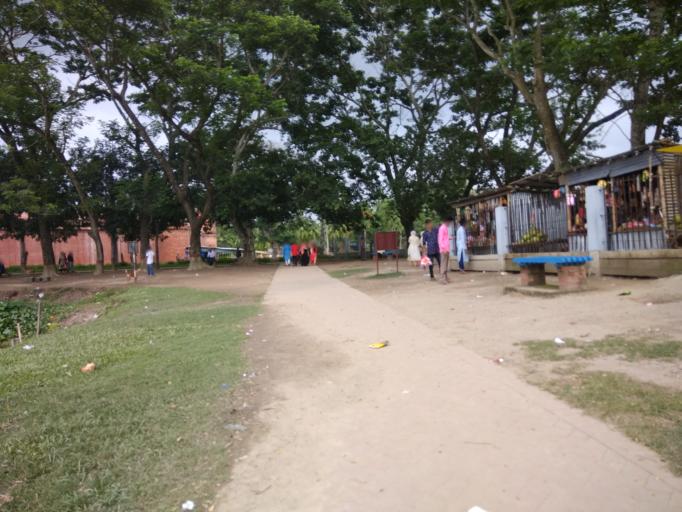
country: BD
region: Khulna
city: Khulna
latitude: 22.6742
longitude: 89.7410
